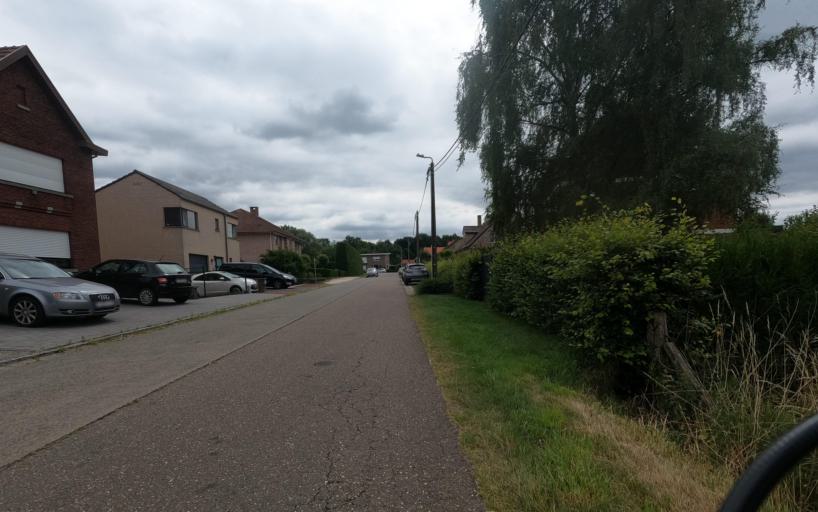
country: BE
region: Flanders
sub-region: Provincie Vlaams-Brabant
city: Aarschot
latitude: 50.9639
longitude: 4.7985
